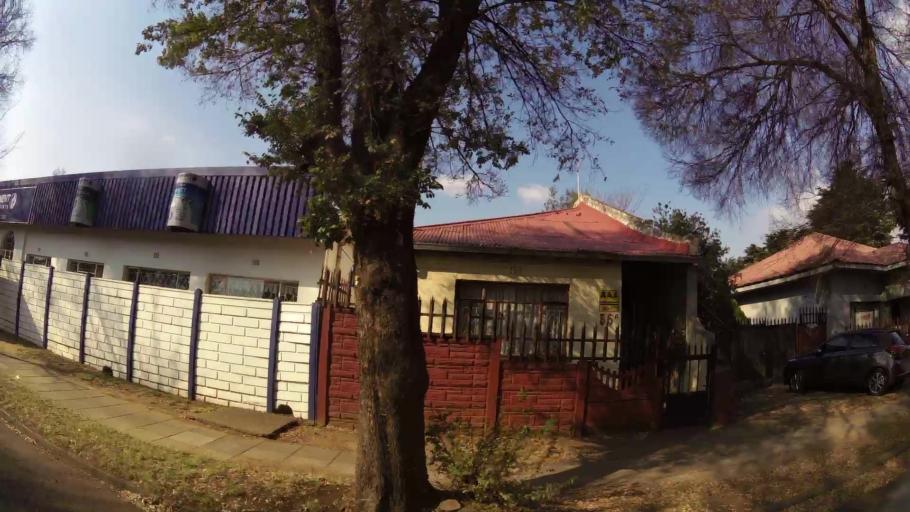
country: ZA
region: Gauteng
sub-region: Ekurhuleni Metropolitan Municipality
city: Boksburg
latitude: -26.2025
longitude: 28.2538
